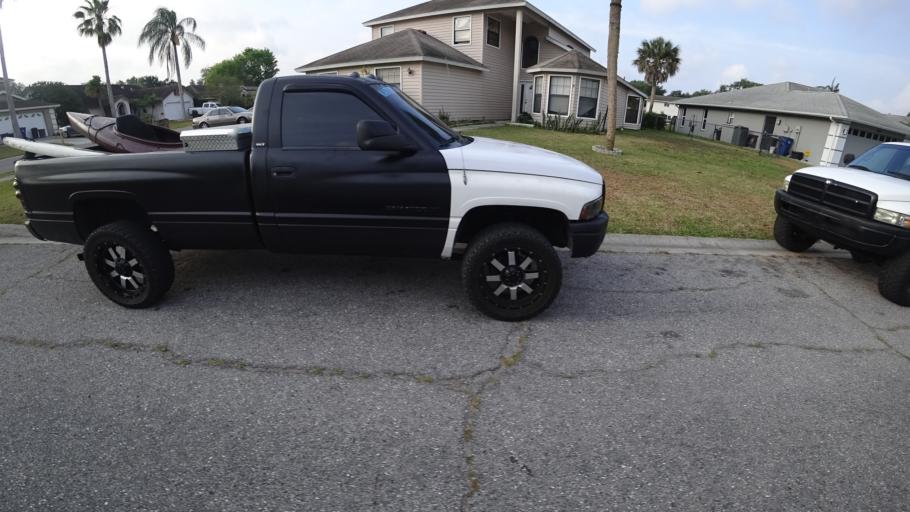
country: US
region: Florida
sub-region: Manatee County
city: Samoset
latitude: 27.4414
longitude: -82.5254
